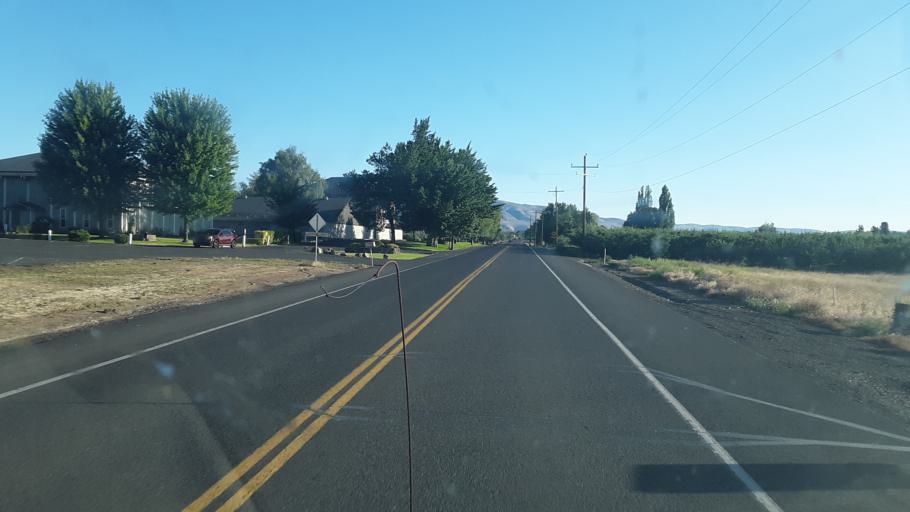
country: US
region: Washington
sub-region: Yakima County
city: Tieton
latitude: 46.6556
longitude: -120.7098
